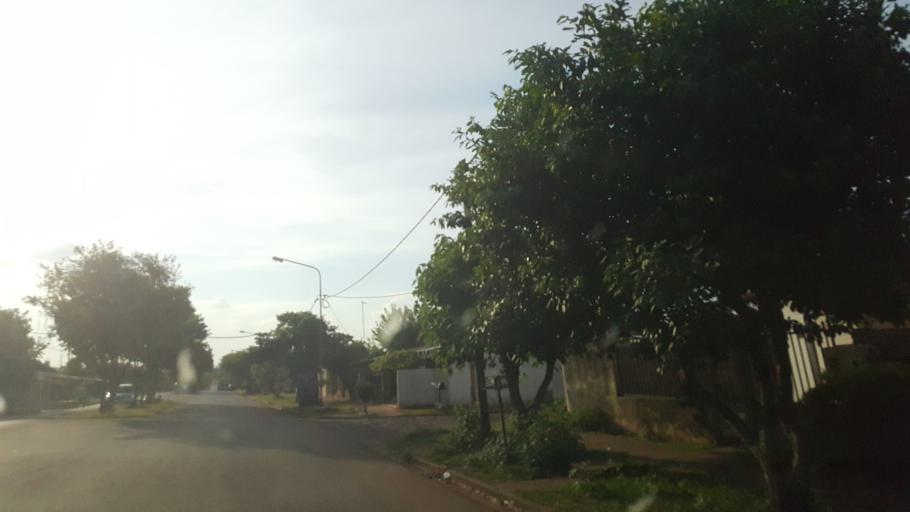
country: AR
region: Misiones
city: Garupa
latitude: -27.4345
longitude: -55.8685
